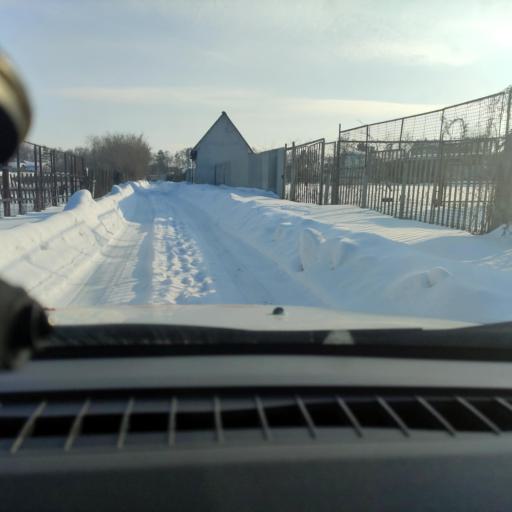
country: RU
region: Samara
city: Samara
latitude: 53.1314
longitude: 50.2589
